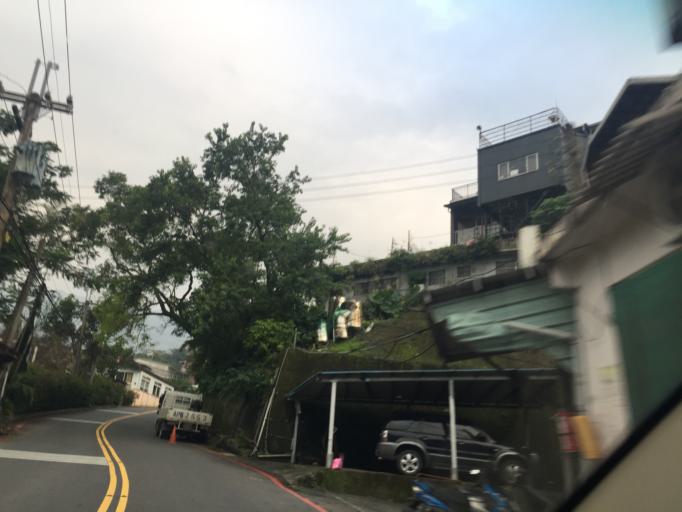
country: TW
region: Taipei
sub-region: Taipei
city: Banqiao
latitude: 24.8631
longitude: 121.5488
